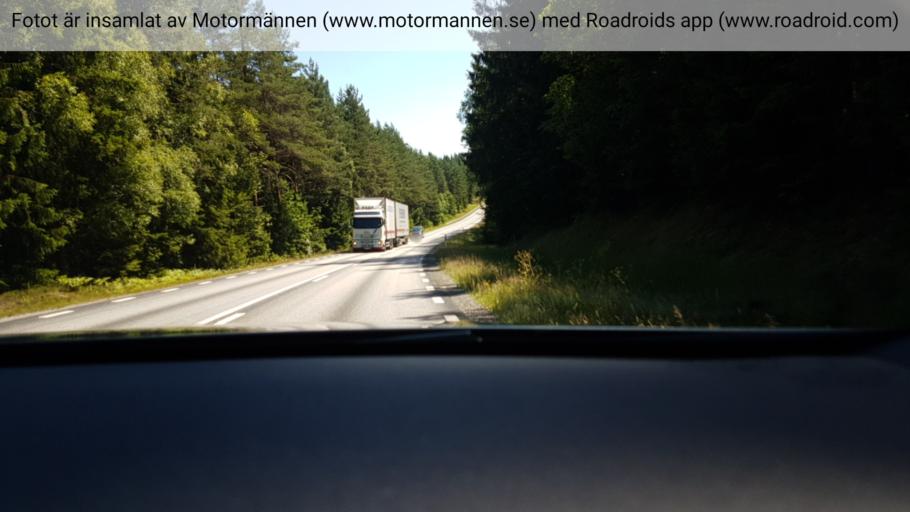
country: SE
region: Joenkoeping
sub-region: Gnosjo Kommun
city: Hillerstorp
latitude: 57.3305
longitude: 13.8214
